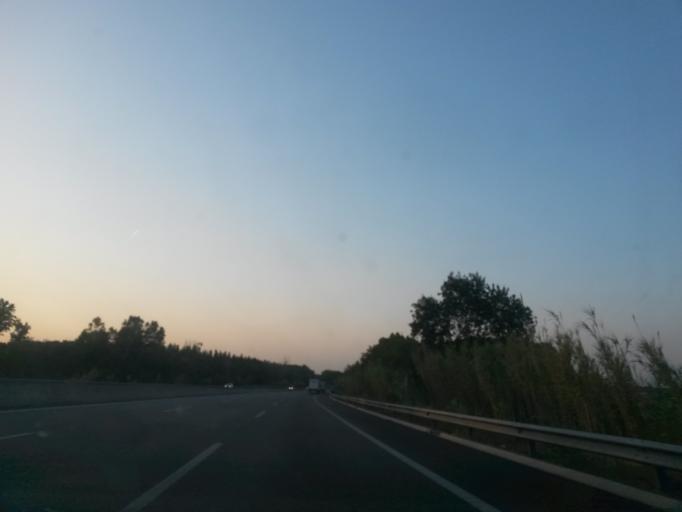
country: ES
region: Catalonia
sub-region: Provincia de Girona
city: Sils
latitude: 41.8166
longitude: 2.7464
